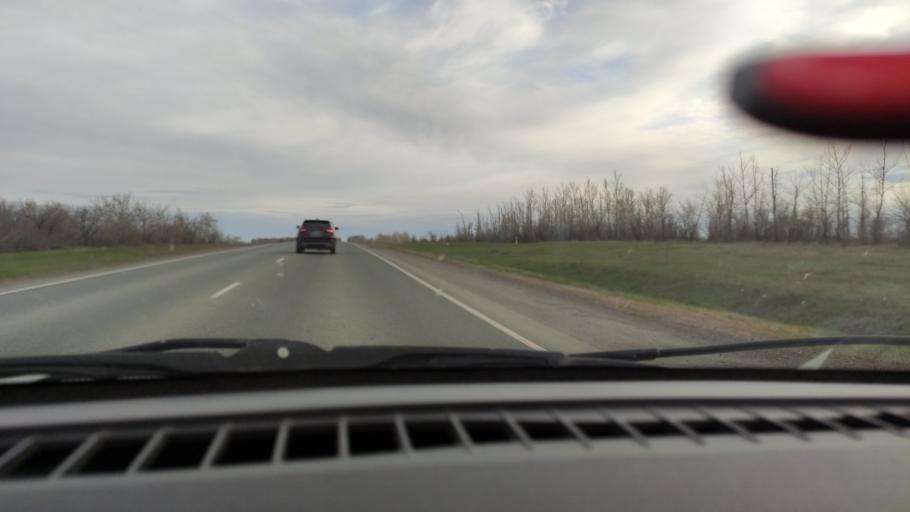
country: RU
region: Orenburg
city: Sakmara
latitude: 52.1600
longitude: 55.2884
